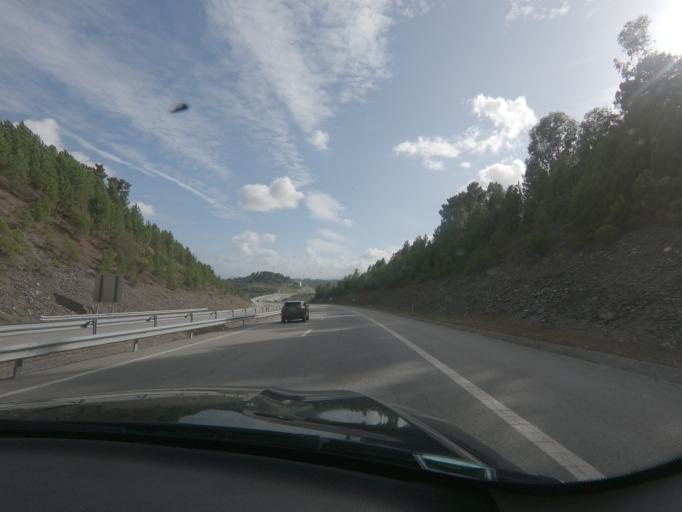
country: PT
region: Vila Real
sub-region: Vila Real
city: Vila Real
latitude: 41.2418
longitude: -7.7254
